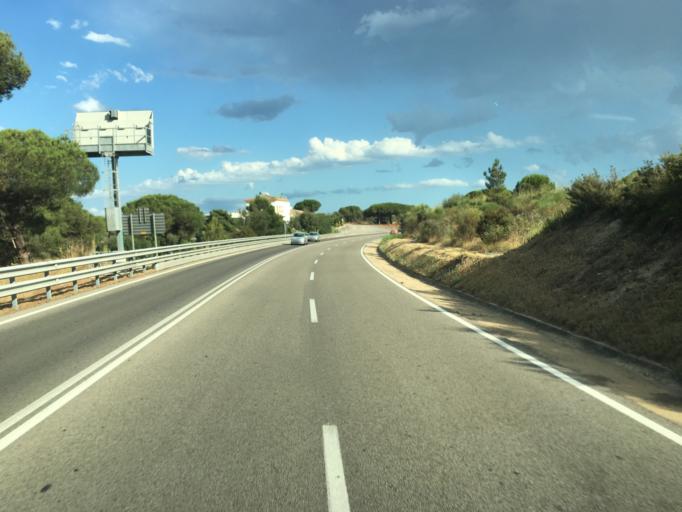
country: ES
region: Catalonia
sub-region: Provincia de Barcelona
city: Palafolls
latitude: 41.6671
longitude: 2.7303
